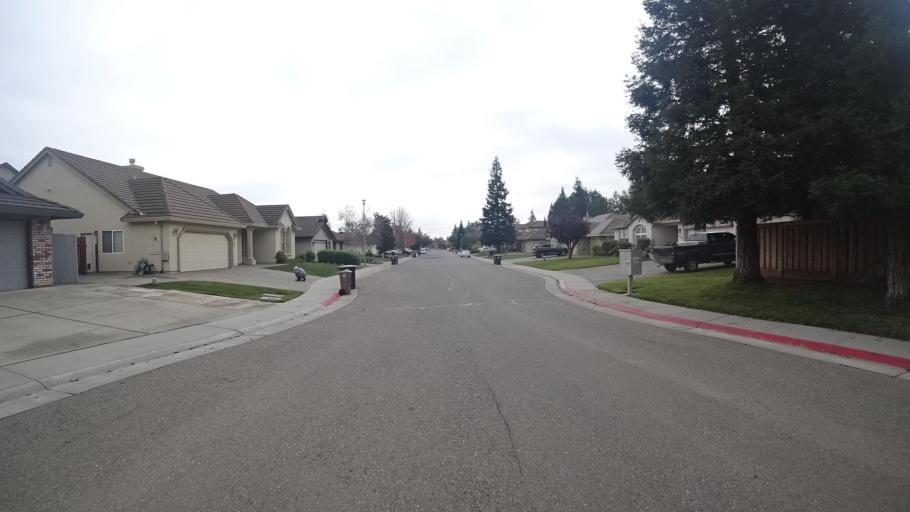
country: US
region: California
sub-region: Sacramento County
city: Elk Grove
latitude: 38.4255
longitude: -121.3649
